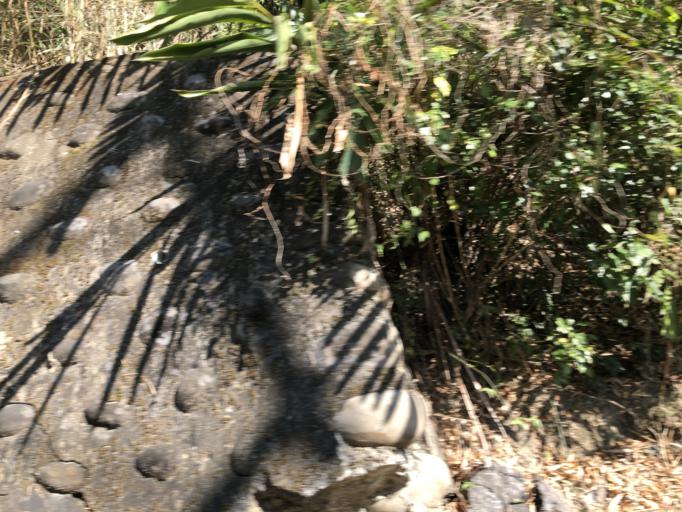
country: TW
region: Taiwan
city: Yujing
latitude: 23.0273
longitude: 120.3854
